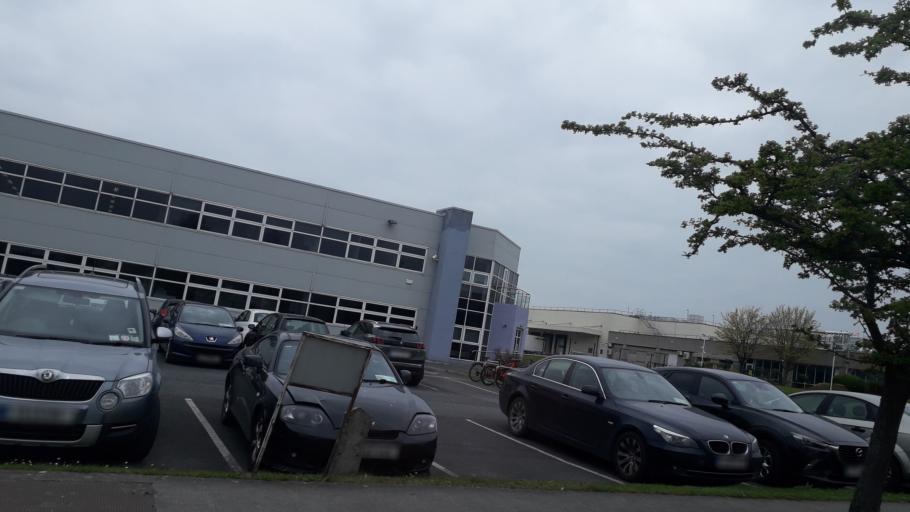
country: IE
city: Bonnybrook
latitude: 53.4022
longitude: -6.2249
